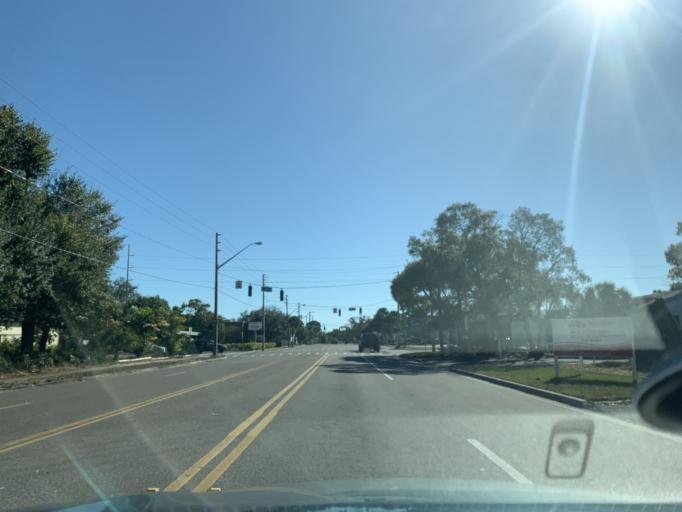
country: US
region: Florida
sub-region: Pinellas County
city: South Pasadena
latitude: 27.7724
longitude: -82.7285
